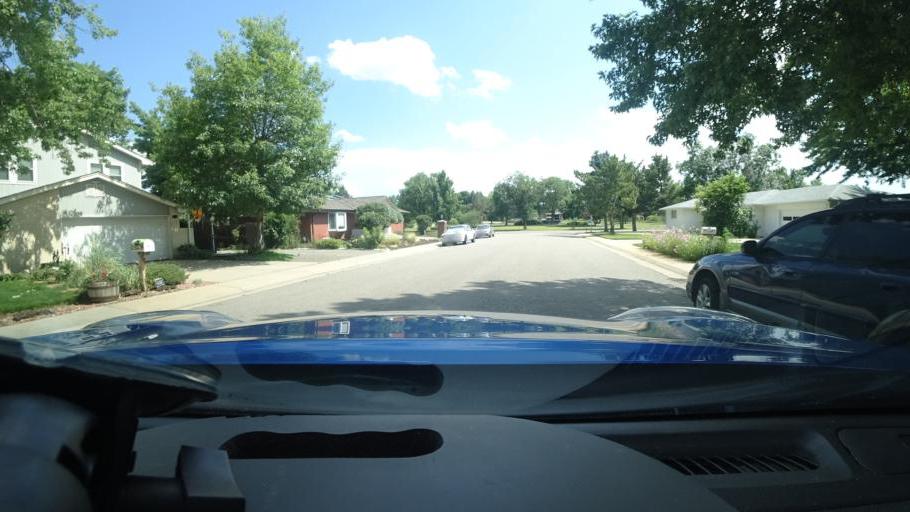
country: US
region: Colorado
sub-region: Adams County
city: Aurora
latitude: 39.6790
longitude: -104.8583
